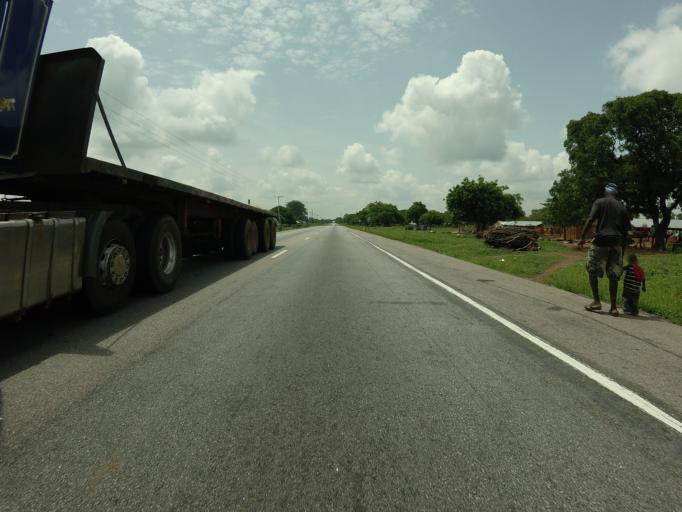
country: GH
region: Northern
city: Tamale
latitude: 9.1291
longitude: -1.2064
